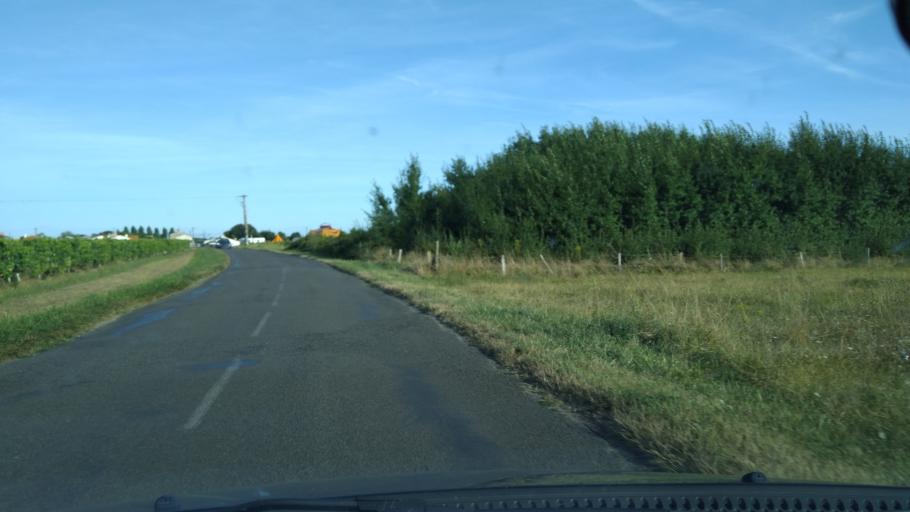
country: FR
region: Poitou-Charentes
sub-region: Departement de la Charente-Maritime
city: Dolus-d'Oleron
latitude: 45.9322
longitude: -1.3329
